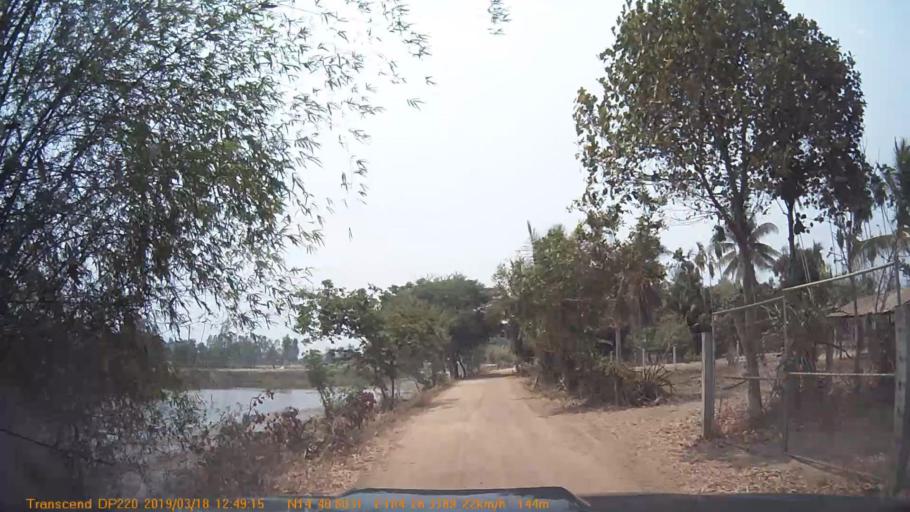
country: TH
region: Sisaket
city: Khun Han
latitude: 14.6767
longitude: 104.4395
